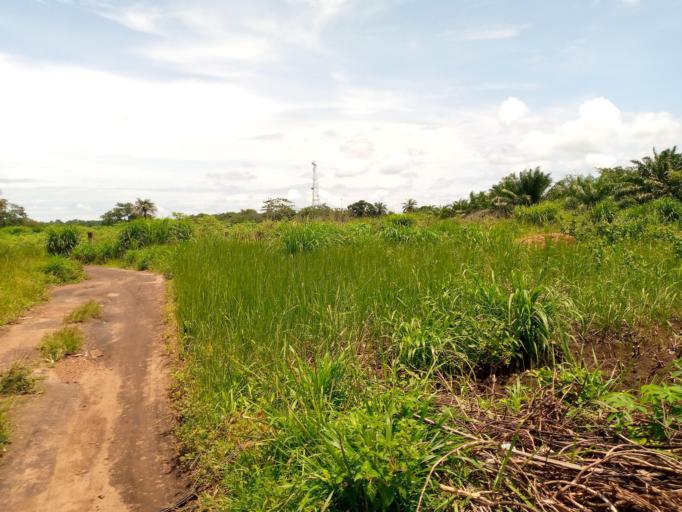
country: SL
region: Northern Province
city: Magburaka
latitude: 8.7237
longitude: -11.9271
